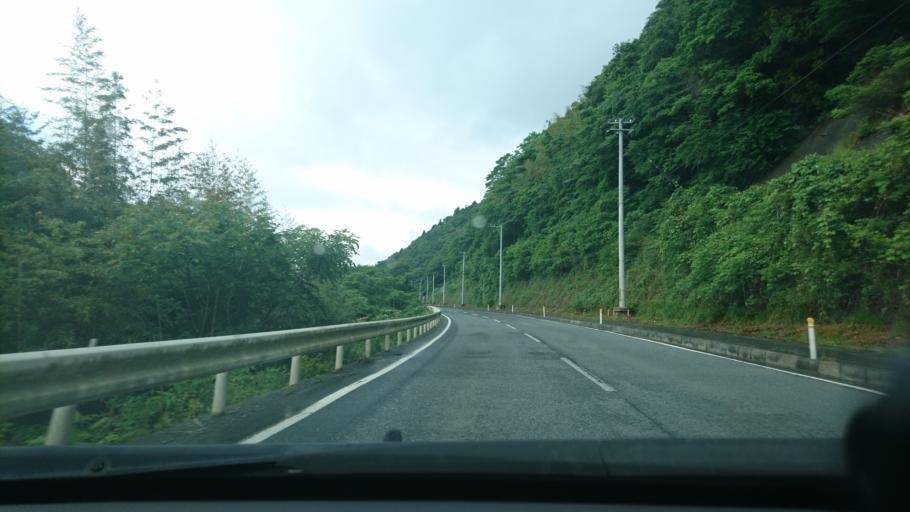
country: JP
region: Miyagi
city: Ishinomaki
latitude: 38.5677
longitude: 141.3007
